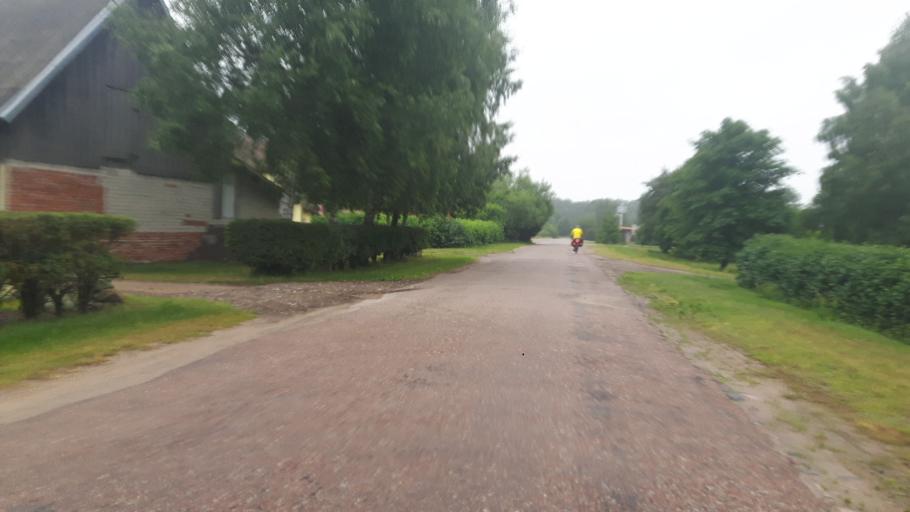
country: LV
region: Nica
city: Nica
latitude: 56.3777
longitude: 20.9879
